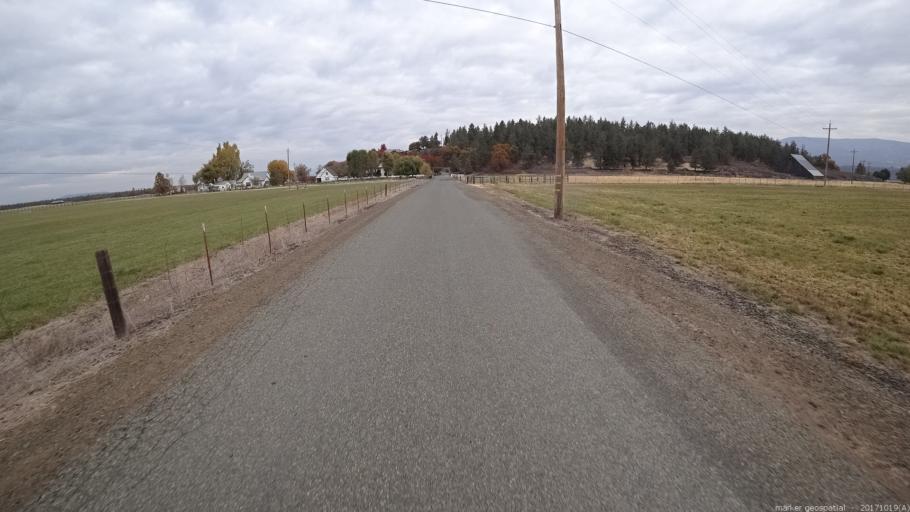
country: US
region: California
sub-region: Shasta County
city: Burney
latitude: 41.0902
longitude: -121.3654
